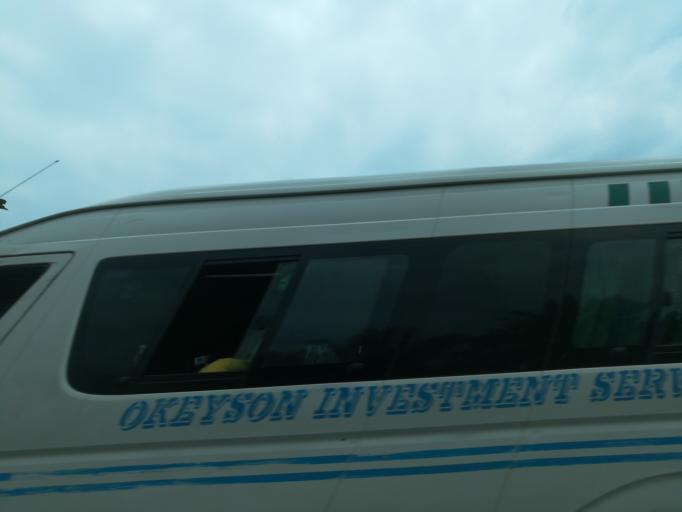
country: NG
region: Lagos
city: Ejirin
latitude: 6.6727
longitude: 3.7997
